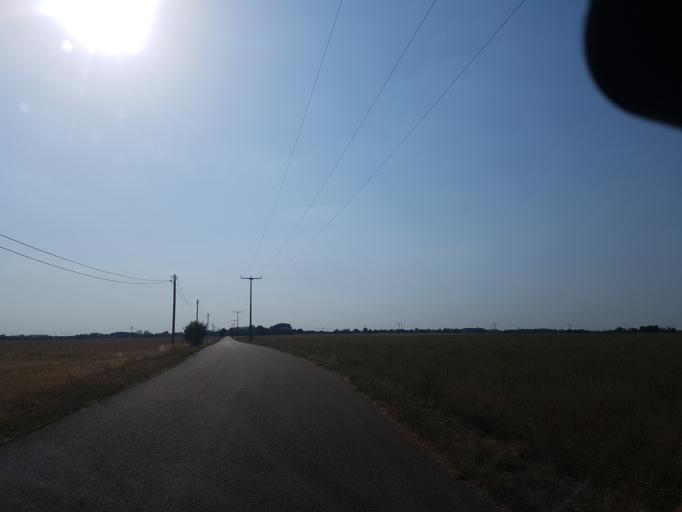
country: DE
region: Saxony
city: Beilrode
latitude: 51.5654
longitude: 13.1018
